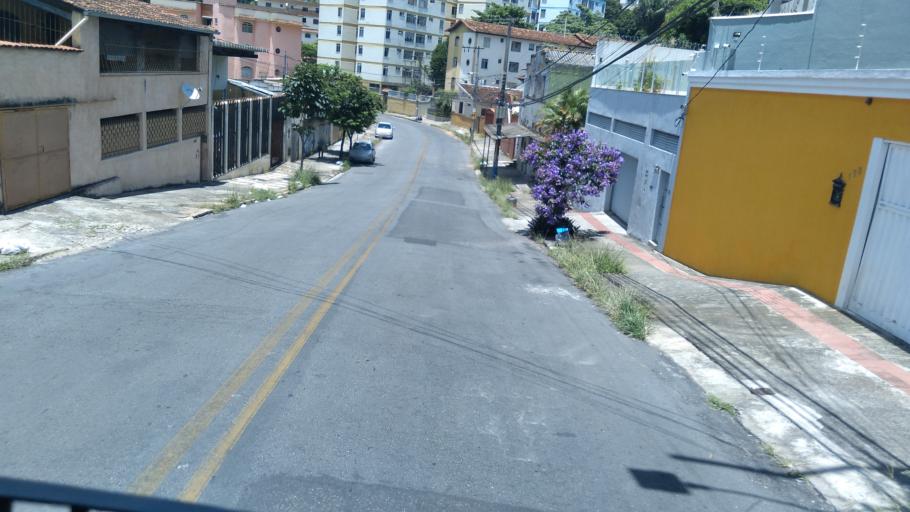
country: BR
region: Minas Gerais
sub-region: Belo Horizonte
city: Belo Horizonte
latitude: -19.9152
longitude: -43.9907
